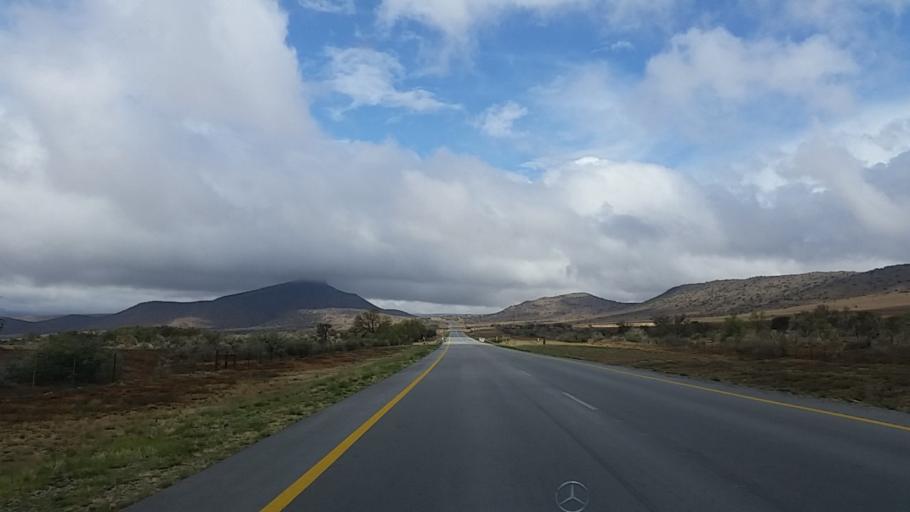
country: ZA
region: Eastern Cape
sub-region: Cacadu District Municipality
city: Graaff-Reinet
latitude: -32.0846
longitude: 24.6023
